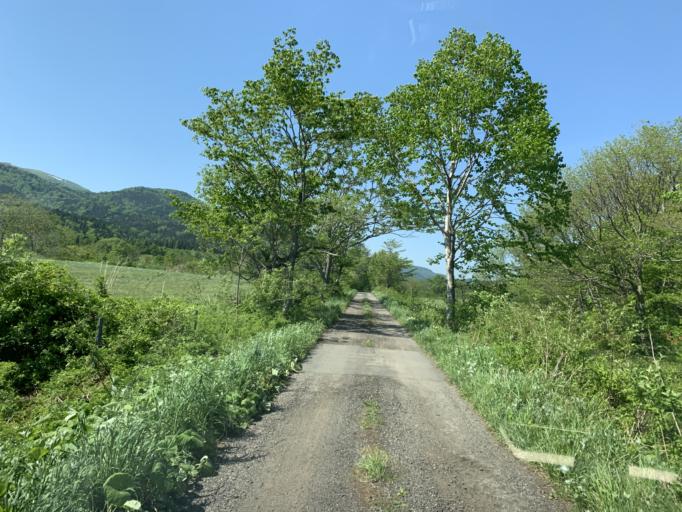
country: JP
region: Iwate
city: Shizukuishi
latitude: 39.5527
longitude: 140.8211
